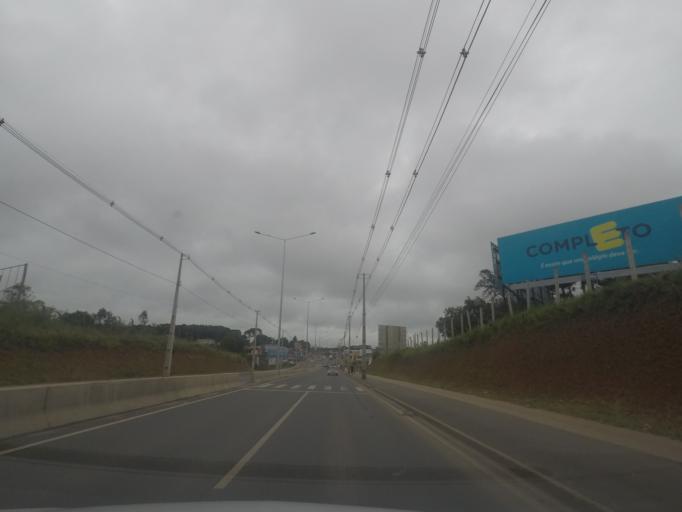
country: BR
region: Parana
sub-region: Piraquara
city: Piraquara
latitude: -25.4549
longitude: -49.0752
